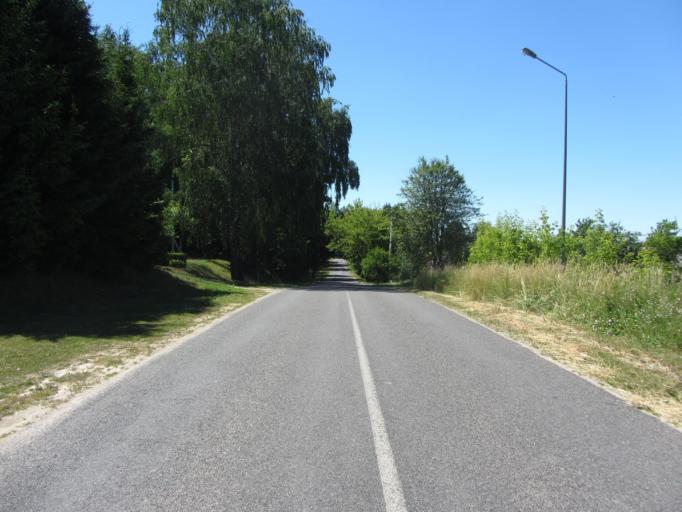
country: LT
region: Vilnius County
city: Elektrenai
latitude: 54.7934
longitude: 24.7039
